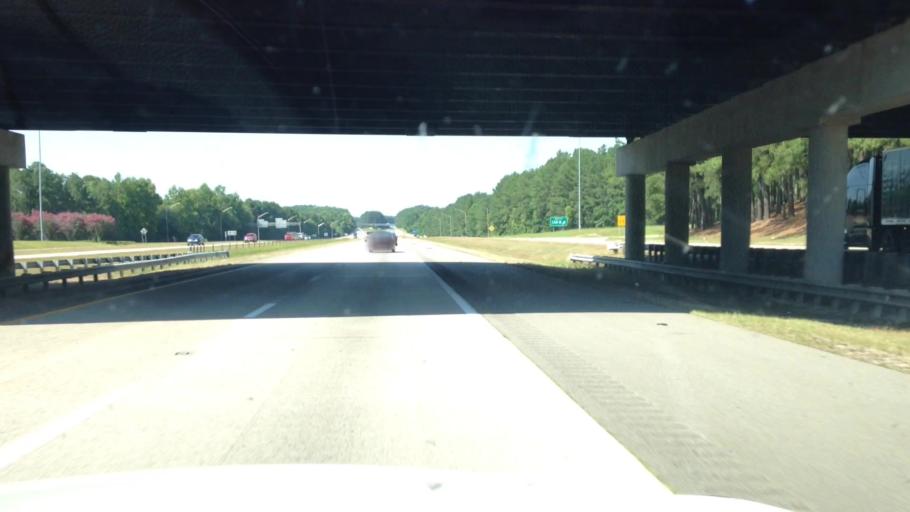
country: US
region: North Carolina
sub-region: Nash County
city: Red Oak
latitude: 35.9821
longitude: -77.8766
